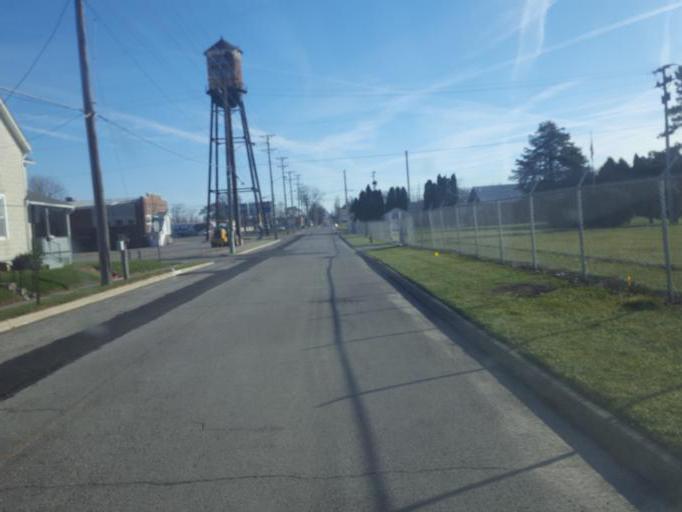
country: US
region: Ohio
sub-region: Crawford County
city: Bucyrus
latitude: 40.7976
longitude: -82.9670
